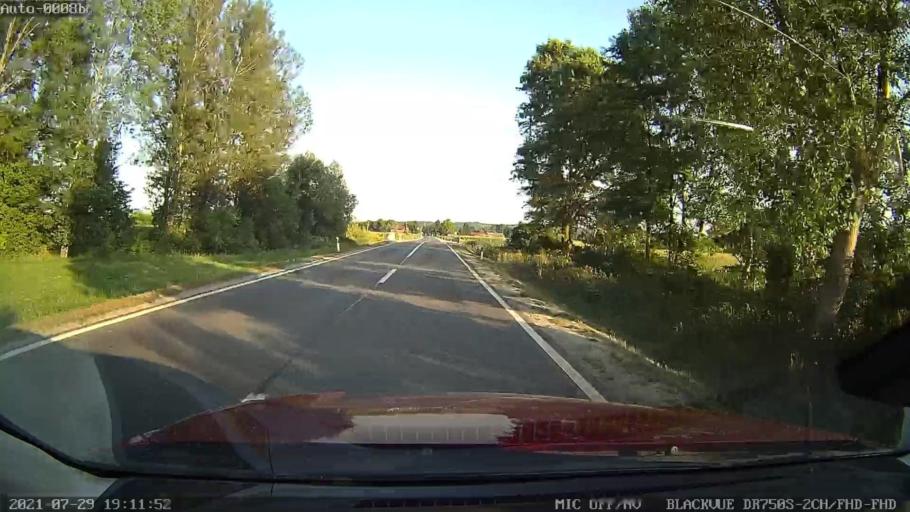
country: HR
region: Varazdinska
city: Jalzabet
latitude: 46.2731
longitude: 16.5123
